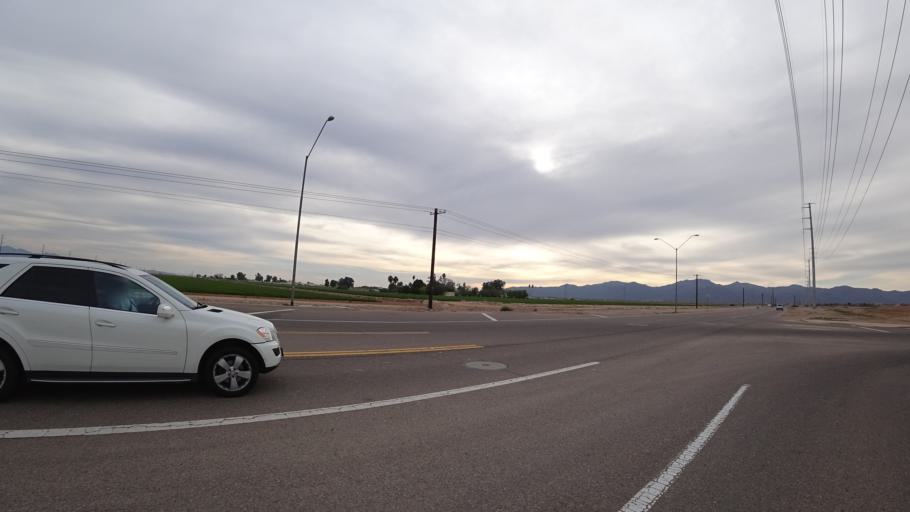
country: US
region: Arizona
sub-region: Maricopa County
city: Citrus Park
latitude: 33.5954
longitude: -112.4222
